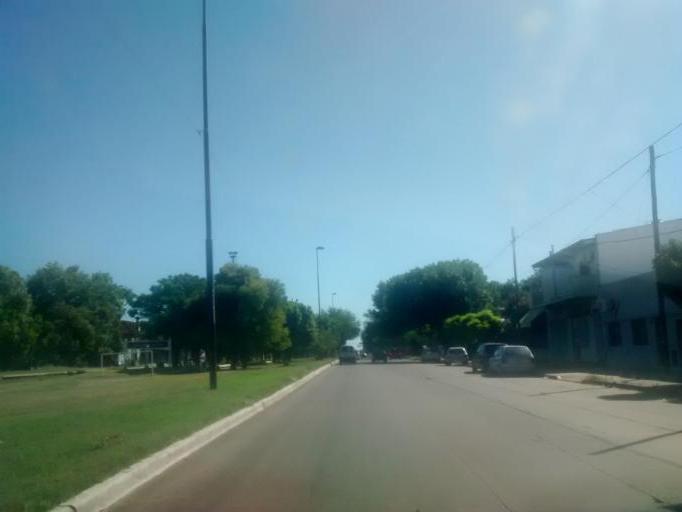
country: AR
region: Buenos Aires
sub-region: Partido de La Plata
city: La Plata
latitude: -34.9348
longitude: -57.9320
